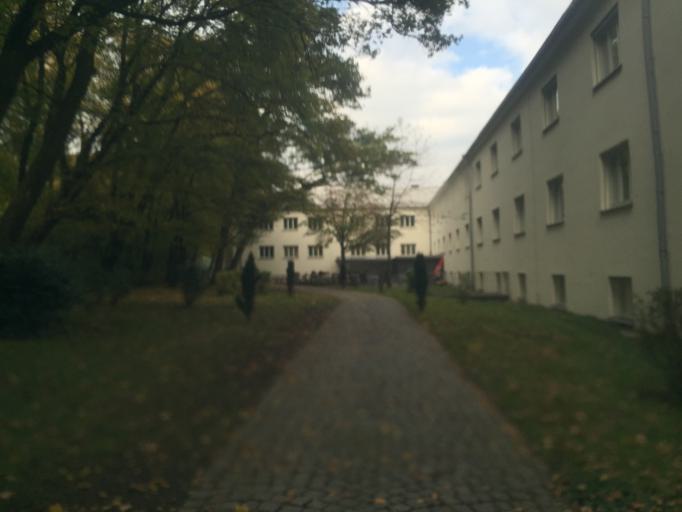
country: DE
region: Bavaria
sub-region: Upper Bavaria
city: Munich
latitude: 48.1492
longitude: 11.5939
